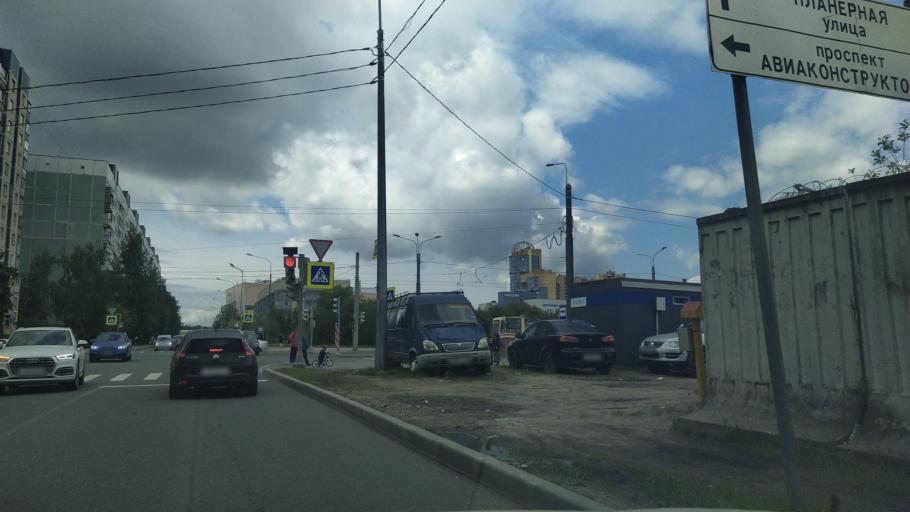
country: RU
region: Leningrad
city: Untolovo
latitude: 60.0232
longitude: 30.2321
